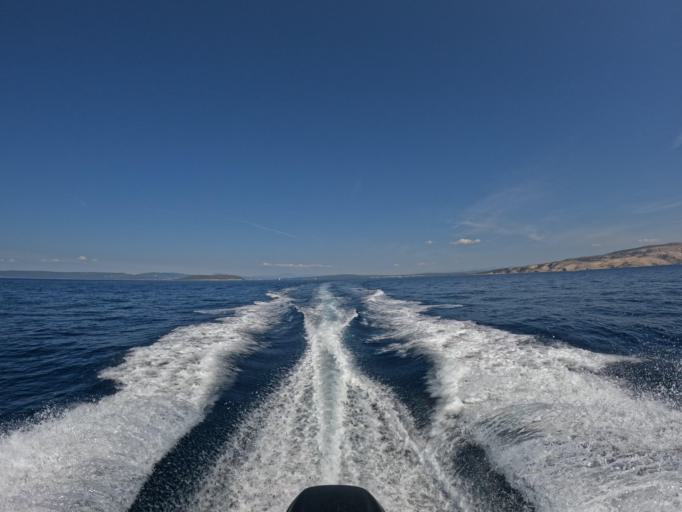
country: HR
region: Primorsko-Goranska
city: Punat
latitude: 44.9195
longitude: 14.6226
